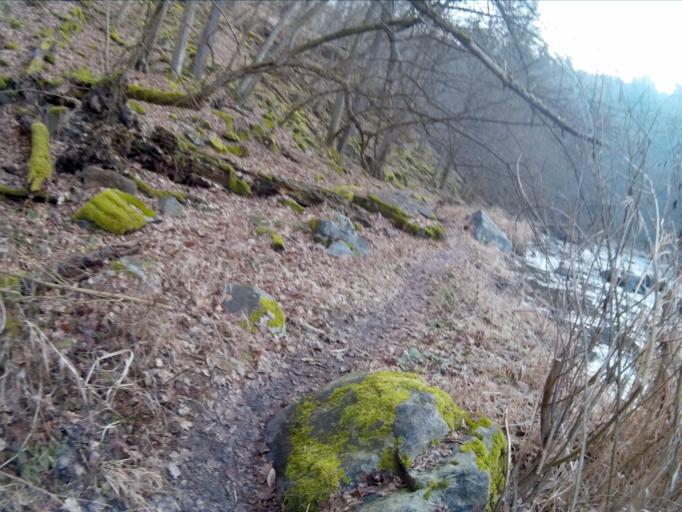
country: CZ
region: Vysocina
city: Namest' nad Oslavou
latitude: 49.1763
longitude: 16.1632
